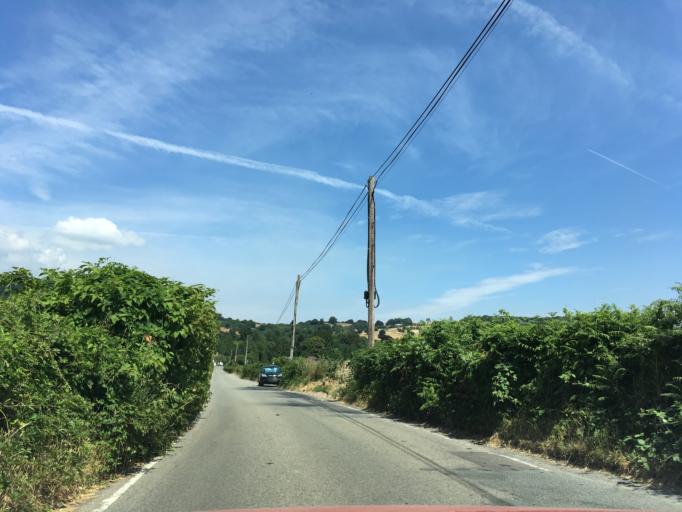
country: GB
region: Wales
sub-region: Caerphilly County Borough
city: Machen
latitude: 51.5825
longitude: -3.1222
